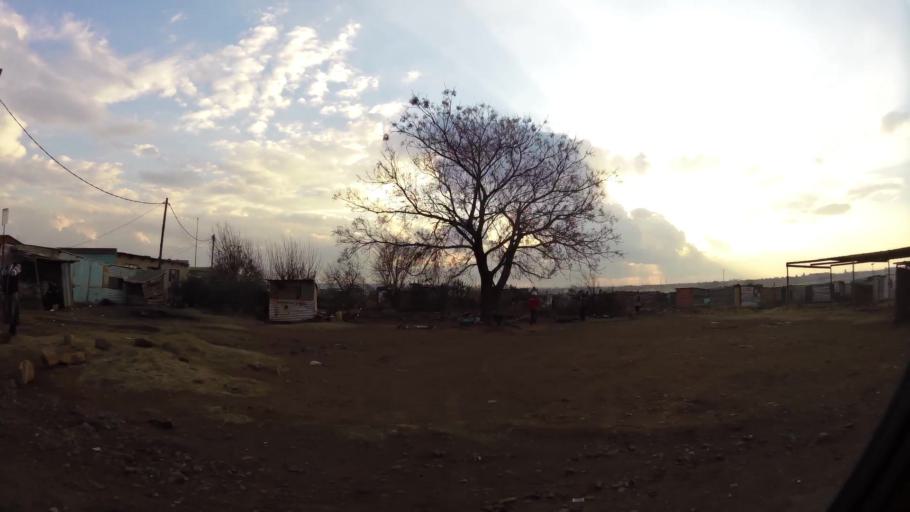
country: ZA
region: Gauteng
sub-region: City of Johannesburg Metropolitan Municipality
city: Orange Farm
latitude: -26.5472
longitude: 27.8334
